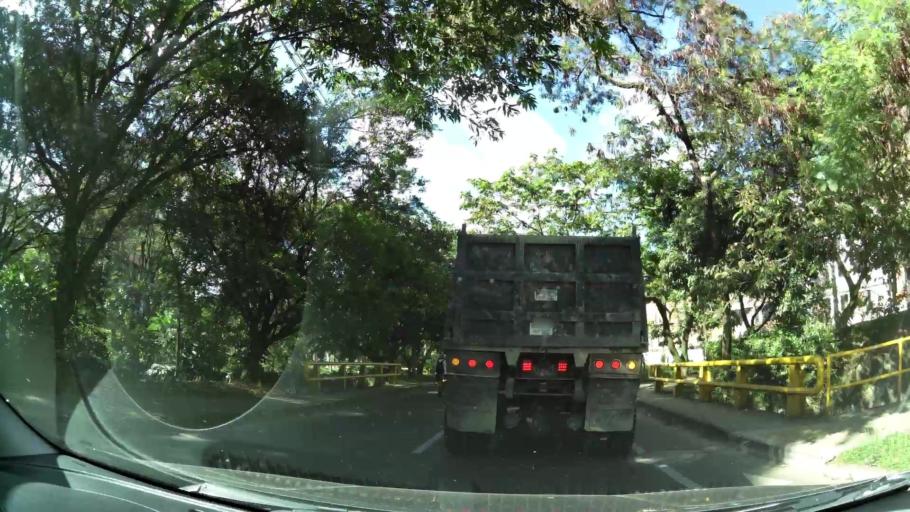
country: CO
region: Antioquia
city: Envigado
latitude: 6.1677
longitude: -75.5804
